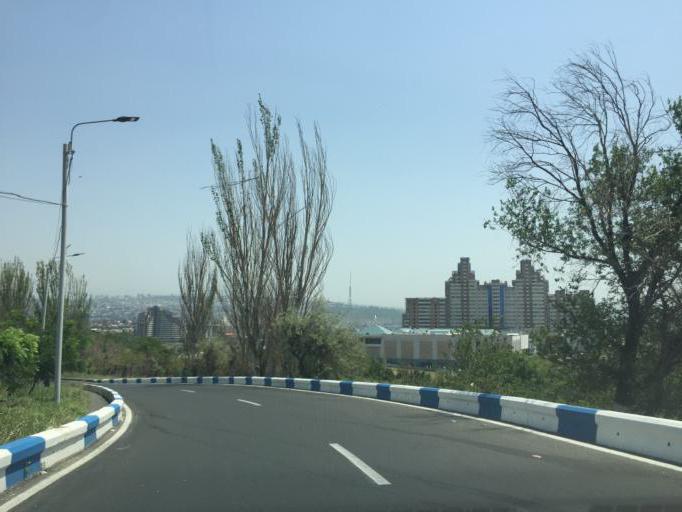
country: AM
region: Yerevan
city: Yerevan
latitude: 40.1811
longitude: 44.4836
